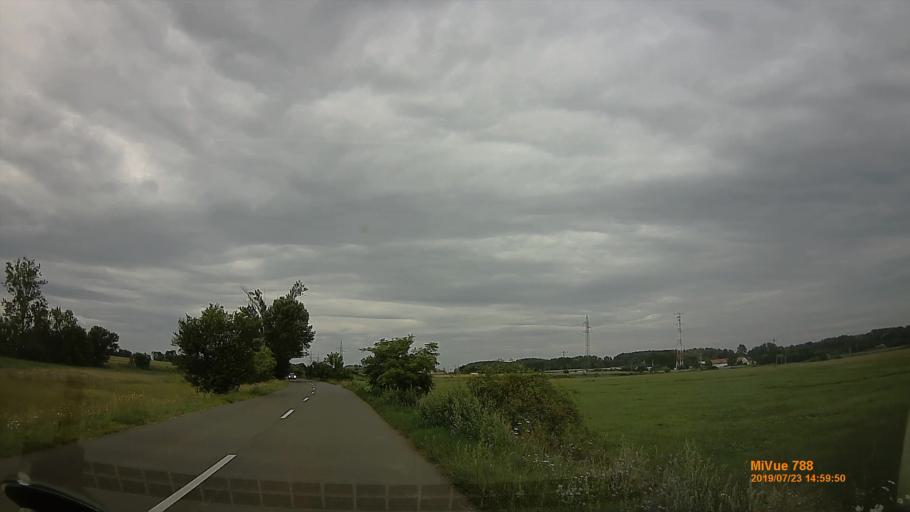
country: HU
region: Szabolcs-Szatmar-Bereg
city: Nyiregyhaza
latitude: 47.9243
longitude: 21.6774
